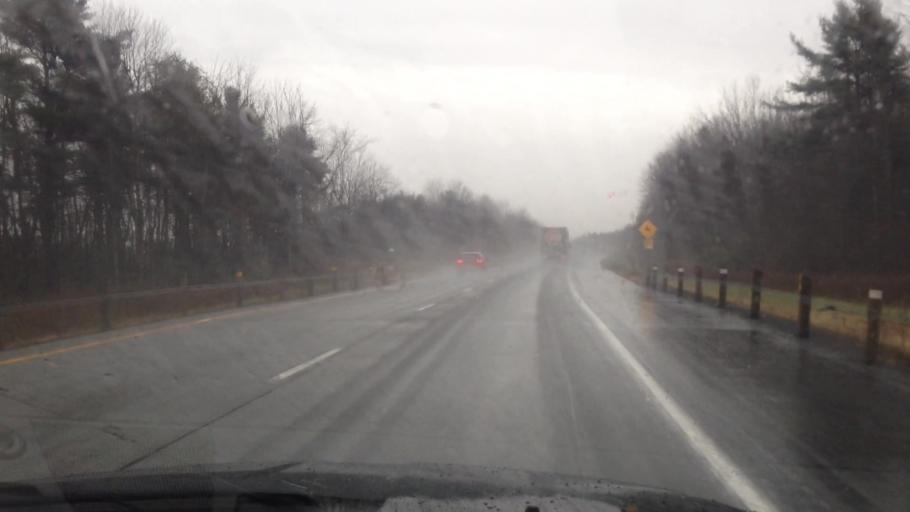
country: CA
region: Ontario
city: Bourget
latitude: 45.3136
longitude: -75.2293
